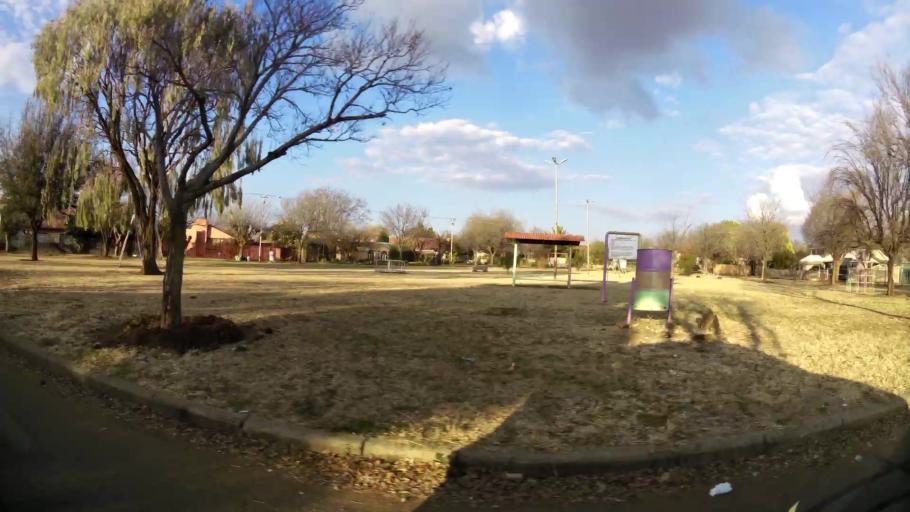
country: ZA
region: Orange Free State
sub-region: Mangaung Metropolitan Municipality
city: Bloemfontein
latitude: -29.1410
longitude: 26.1927
